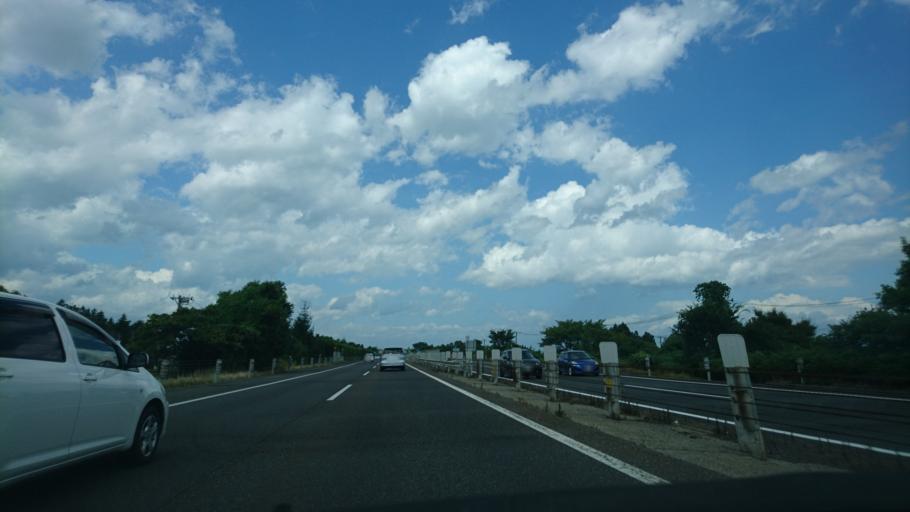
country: JP
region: Iwate
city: Morioka-shi
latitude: 39.6287
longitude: 141.1281
